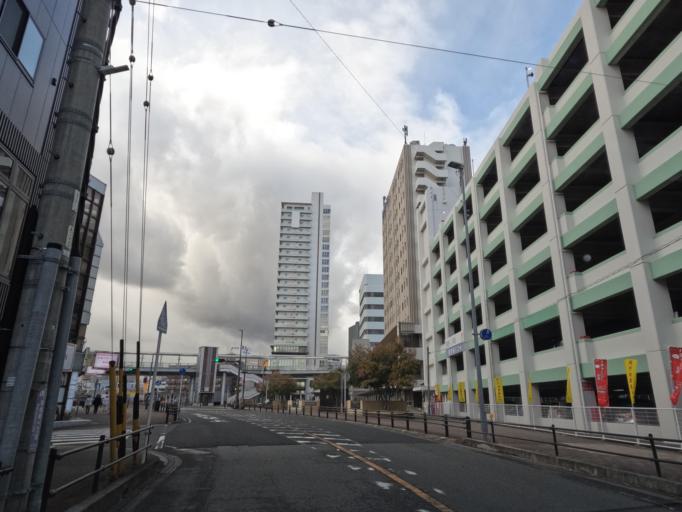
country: JP
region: Aichi
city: Chiryu
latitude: 34.9902
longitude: 137.0094
